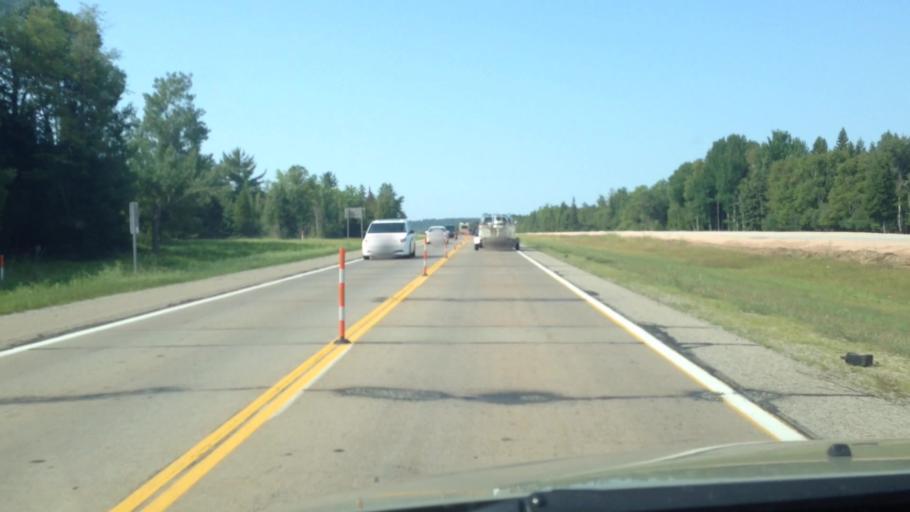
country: US
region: Michigan
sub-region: Delta County
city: Gladstone
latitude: 45.8878
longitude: -87.0061
